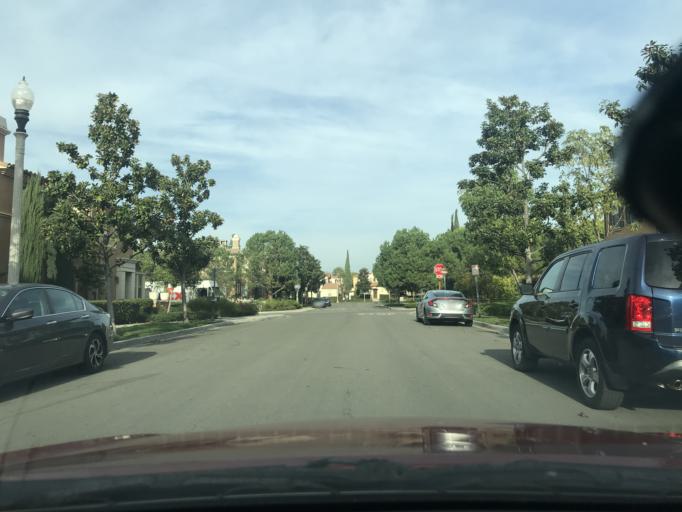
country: US
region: California
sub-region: Orange County
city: North Tustin
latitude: 33.7001
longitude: -117.7506
